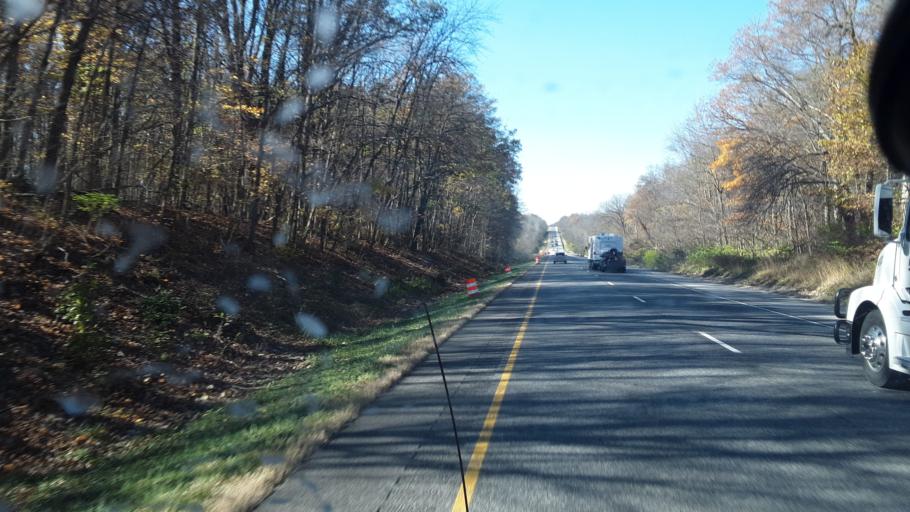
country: US
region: Indiana
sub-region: Henry County
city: New Castle
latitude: 39.8538
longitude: -85.4348
